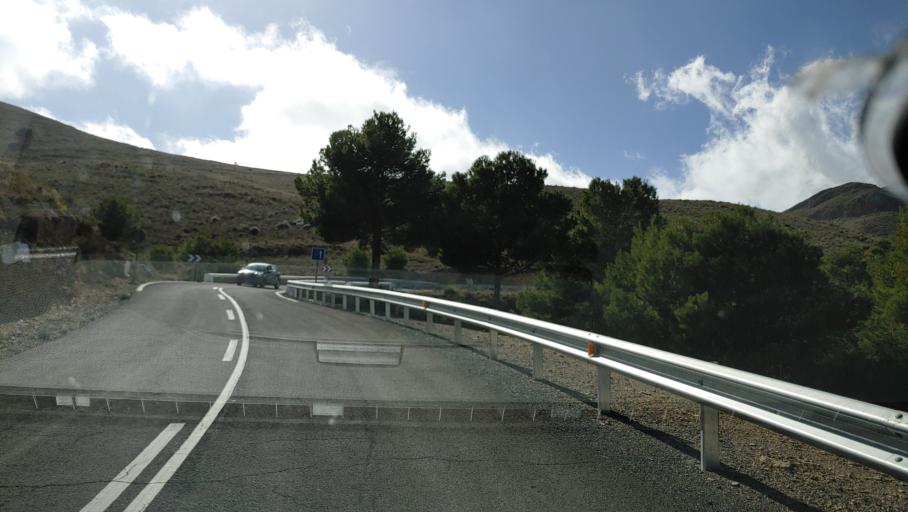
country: ES
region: Andalusia
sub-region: Provincia de Almeria
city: Enix
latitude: 36.9183
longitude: -2.5974
